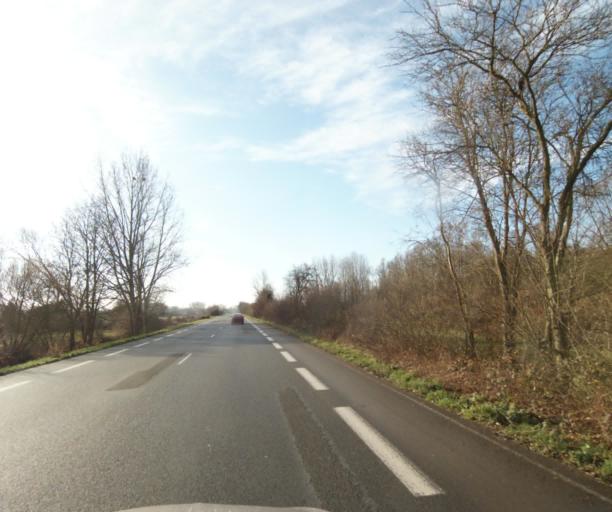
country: FR
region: Nord-Pas-de-Calais
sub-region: Departement du Nord
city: Trith-Saint-Leger
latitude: 50.3198
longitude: 3.4896
